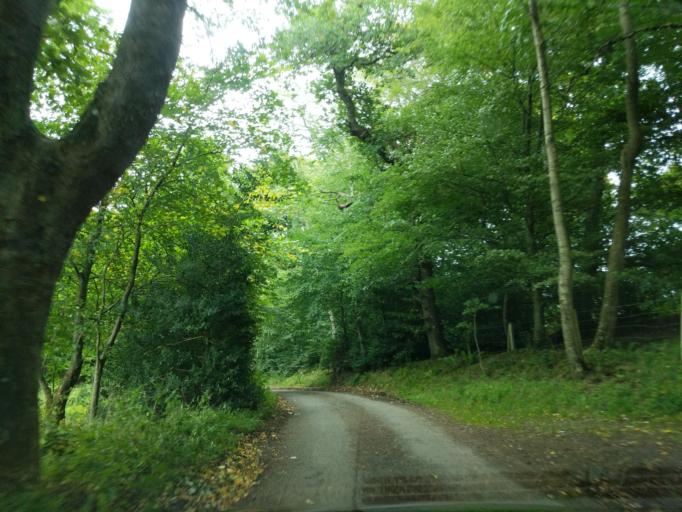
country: GB
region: Scotland
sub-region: The Scottish Borders
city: Galashiels
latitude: 55.5986
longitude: -2.7784
